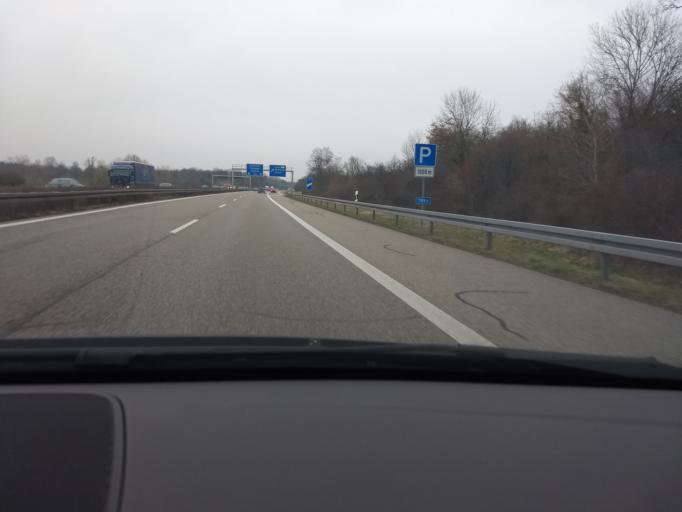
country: FR
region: Alsace
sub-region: Departement du Haut-Rhin
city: Ottmarsheim
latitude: 47.7776
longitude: 7.5359
